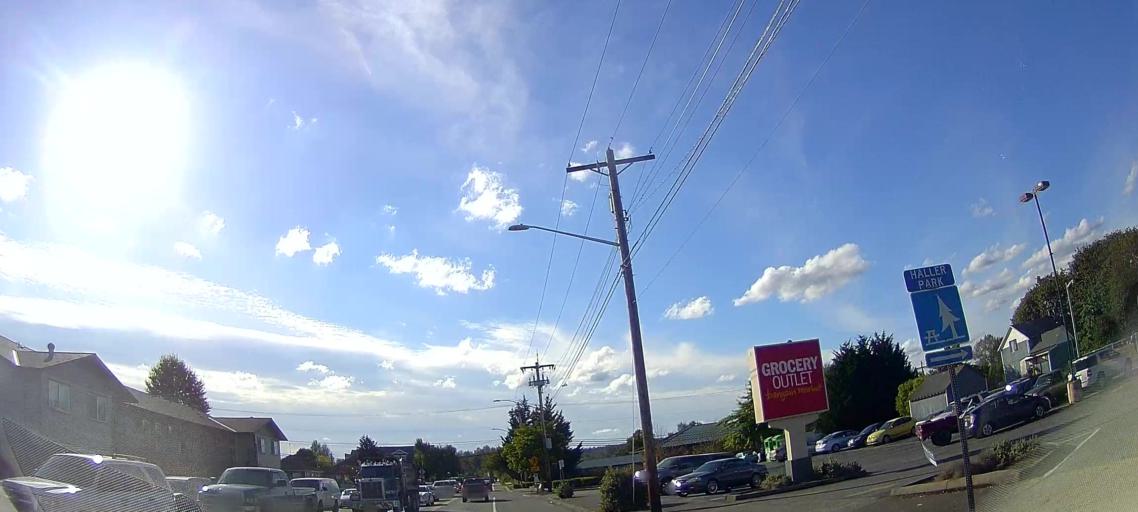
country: US
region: Washington
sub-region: Snohomish County
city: Arlington
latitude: 48.2005
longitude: -122.1270
